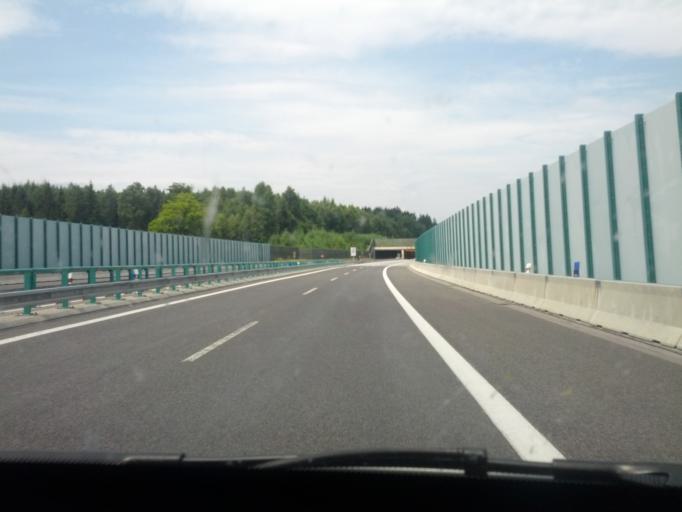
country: DE
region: Saxony
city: Liebstadt
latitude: 50.7833
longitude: 13.8979
